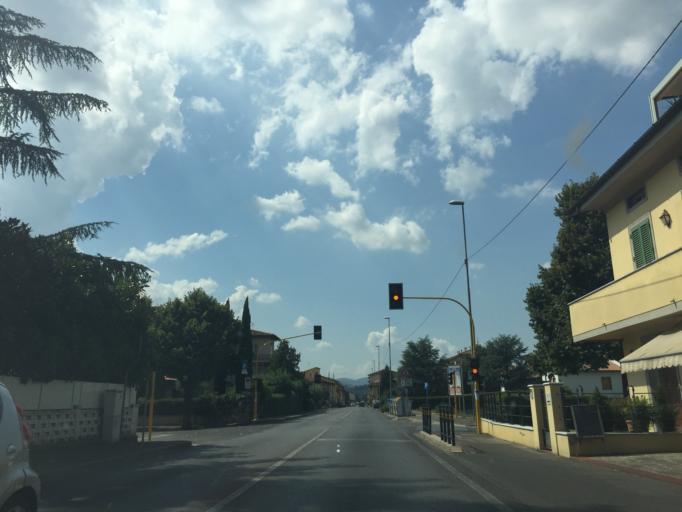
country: IT
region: Tuscany
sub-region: Provincia di Prato
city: Poggio A Caiano
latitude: 43.8115
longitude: 11.0786
